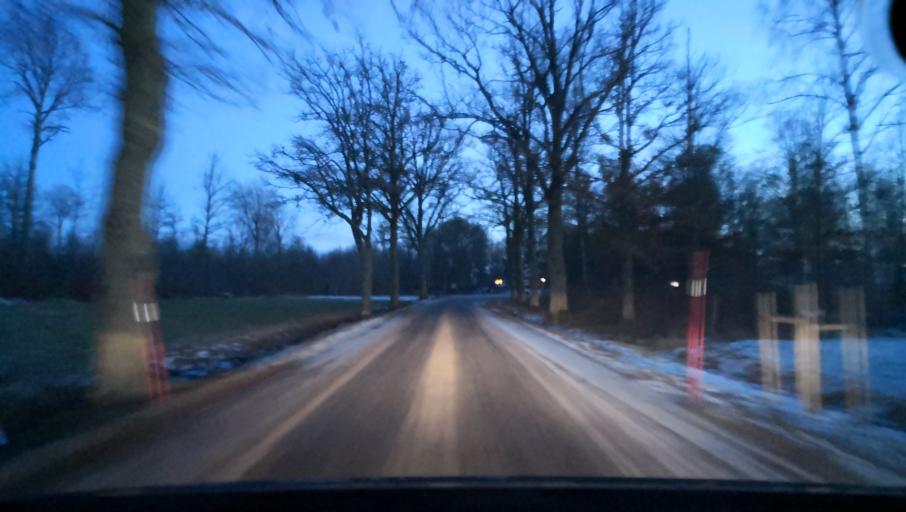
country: SE
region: Soedermanland
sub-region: Katrineholms Kommun
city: Katrineholm
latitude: 59.0742
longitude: 16.3340
